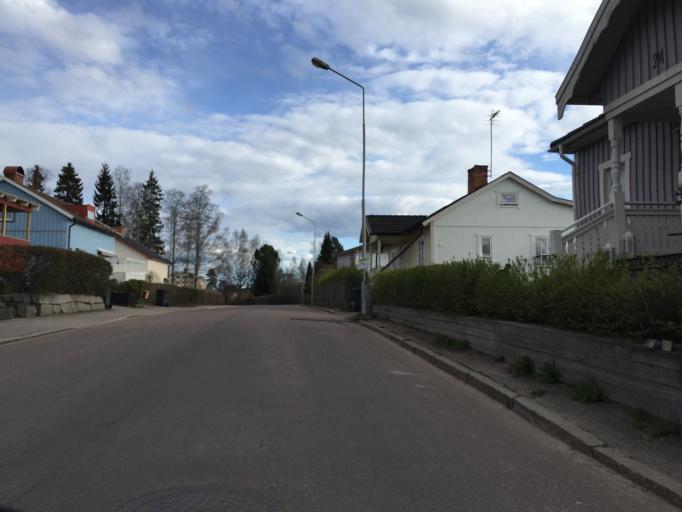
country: SE
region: Dalarna
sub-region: Ludvika Kommun
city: Ludvika
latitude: 60.1362
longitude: 15.1812
